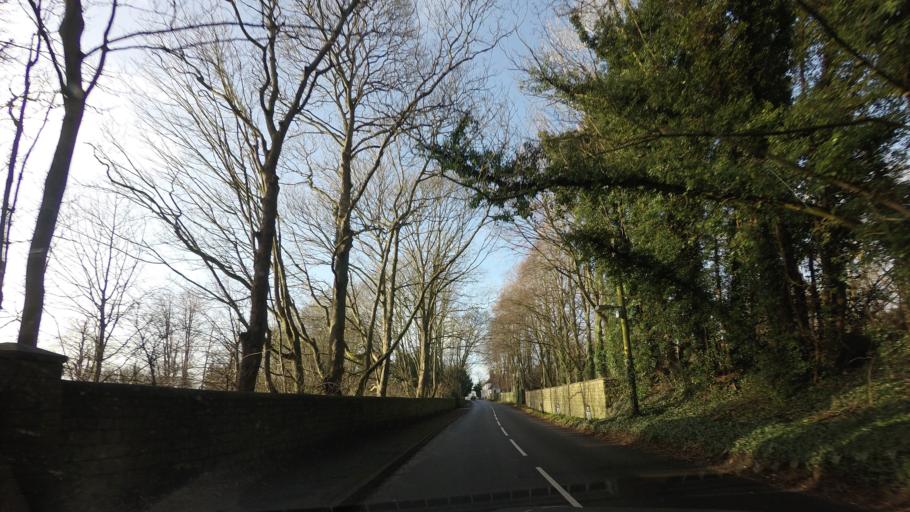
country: GB
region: England
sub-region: Kent
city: Borough Green
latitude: 51.3078
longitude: 0.3135
